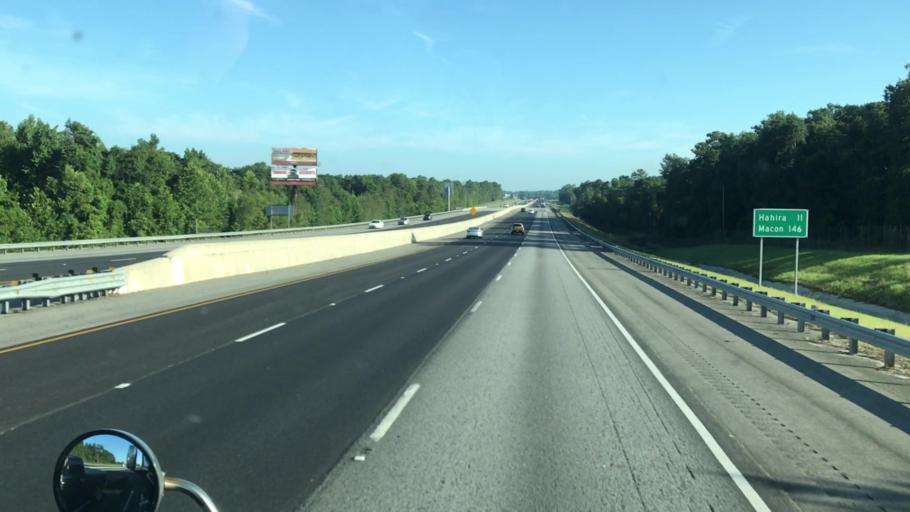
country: US
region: Georgia
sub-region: Lowndes County
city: Remerton
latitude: 30.8511
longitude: -83.3328
